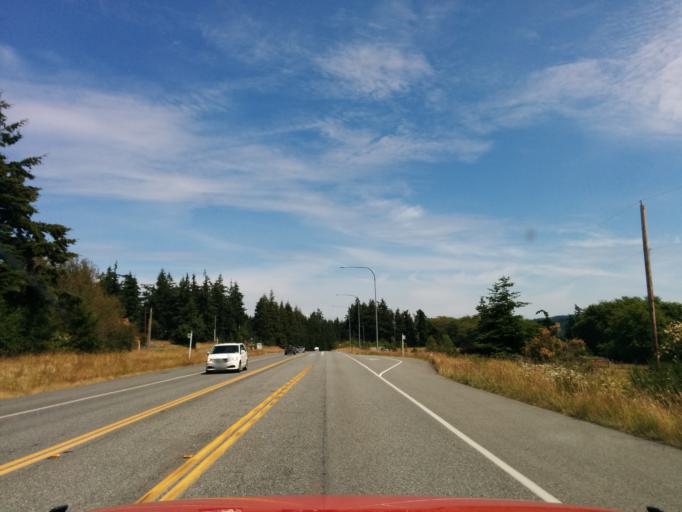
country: US
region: Washington
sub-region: Island County
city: Ault Field
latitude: 48.3581
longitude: -122.6239
